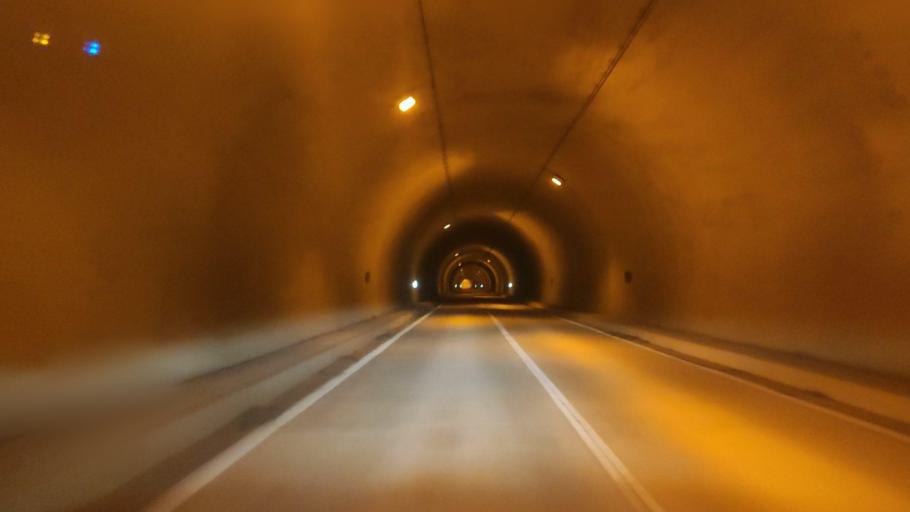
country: JP
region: Kumamoto
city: Matsubase
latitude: 32.5078
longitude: 130.9204
